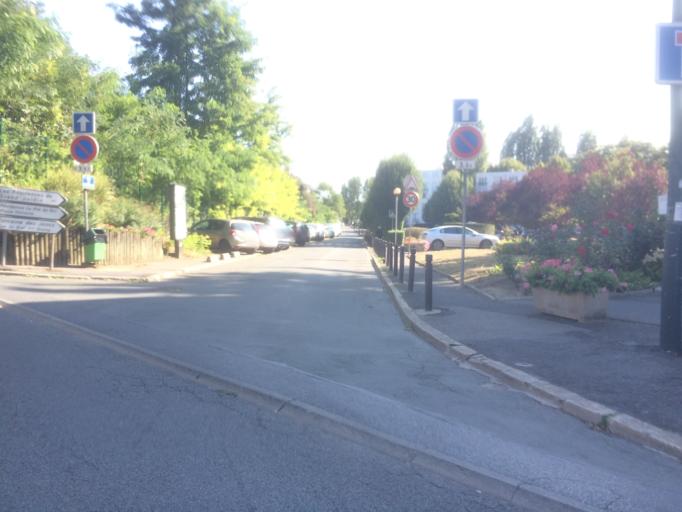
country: FR
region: Ile-de-France
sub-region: Departement de l'Essonne
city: Longjumeau
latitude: 48.6925
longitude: 2.3156
